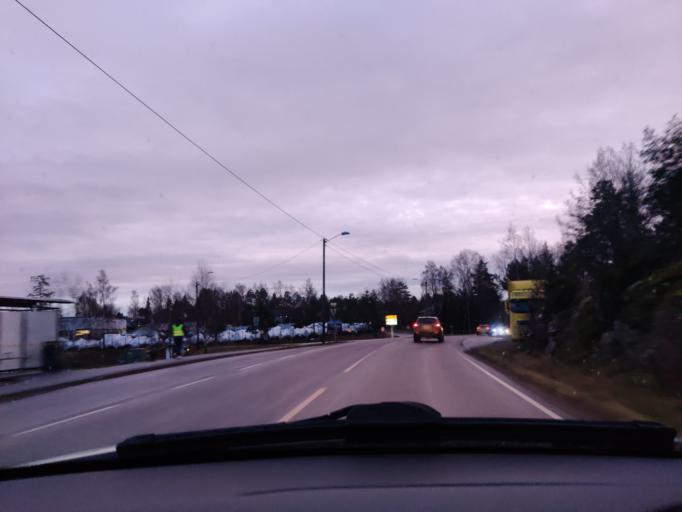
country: NO
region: Vestfold
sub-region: Stokke
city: Melsomvik
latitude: 59.2553
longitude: 10.3584
